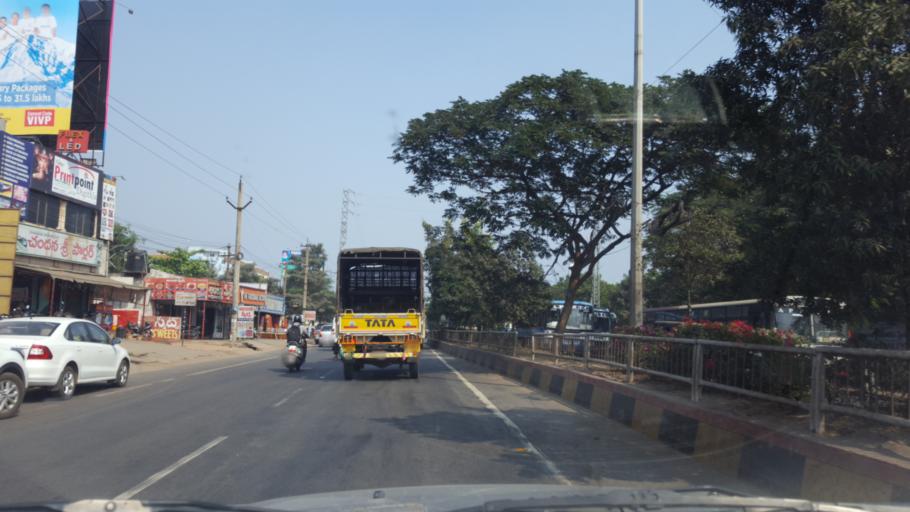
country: IN
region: Andhra Pradesh
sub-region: Vishakhapatnam
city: Visakhapatnam
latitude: 17.6850
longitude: 83.1656
